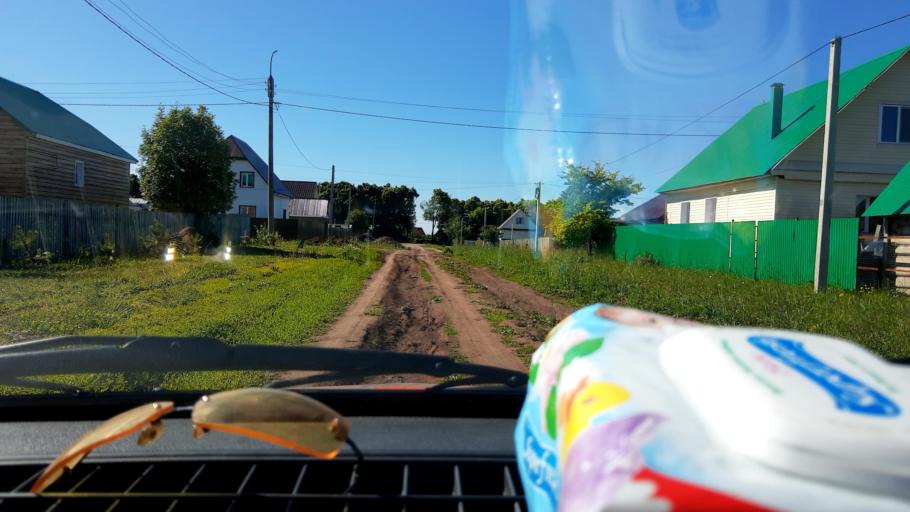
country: RU
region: Bashkortostan
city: Blagoveshchensk
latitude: 55.0645
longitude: 55.9366
